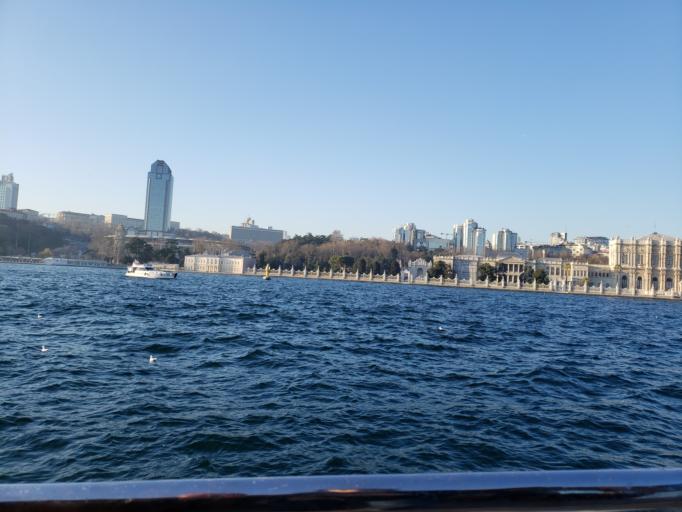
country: TR
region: Istanbul
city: UEskuedar
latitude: 41.0354
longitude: 29.0008
